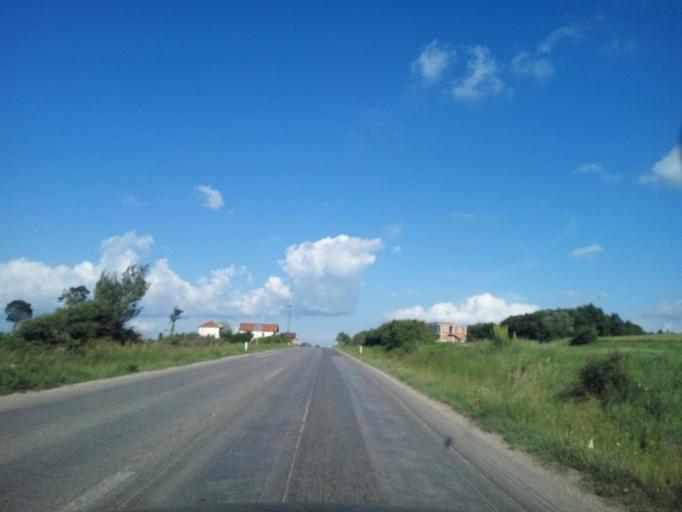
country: XK
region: Prizren
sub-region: Komuna e Malisheves
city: Llazice
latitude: 42.5873
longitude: 20.6771
